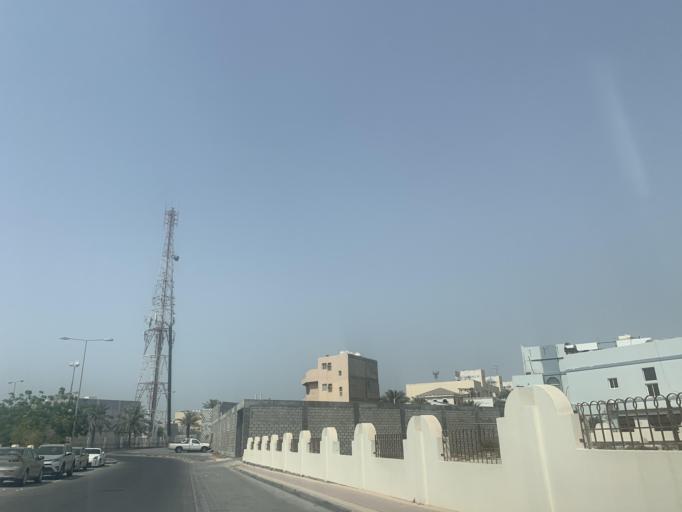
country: BH
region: Manama
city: Jidd Hafs
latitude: 26.2139
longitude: 50.4624
